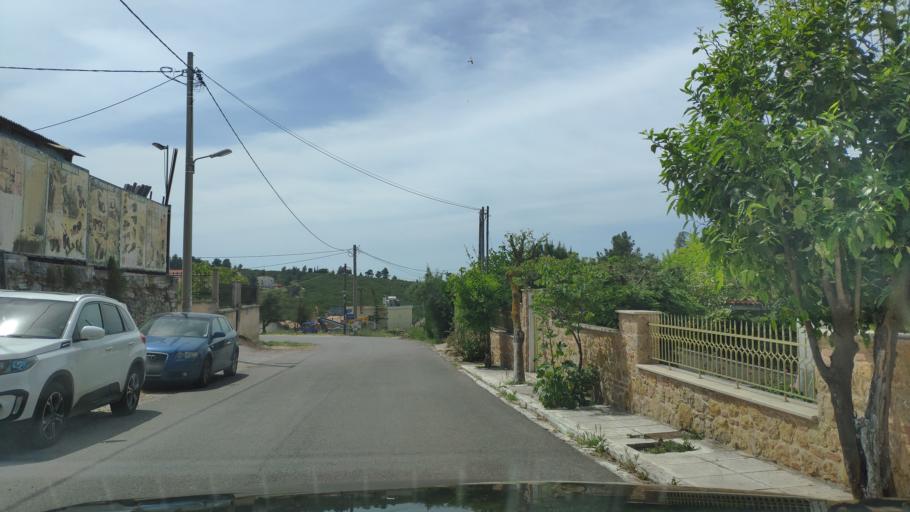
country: GR
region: Attica
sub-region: Nomarchia Anatolikis Attikis
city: Varnavas
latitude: 38.2221
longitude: 23.9245
